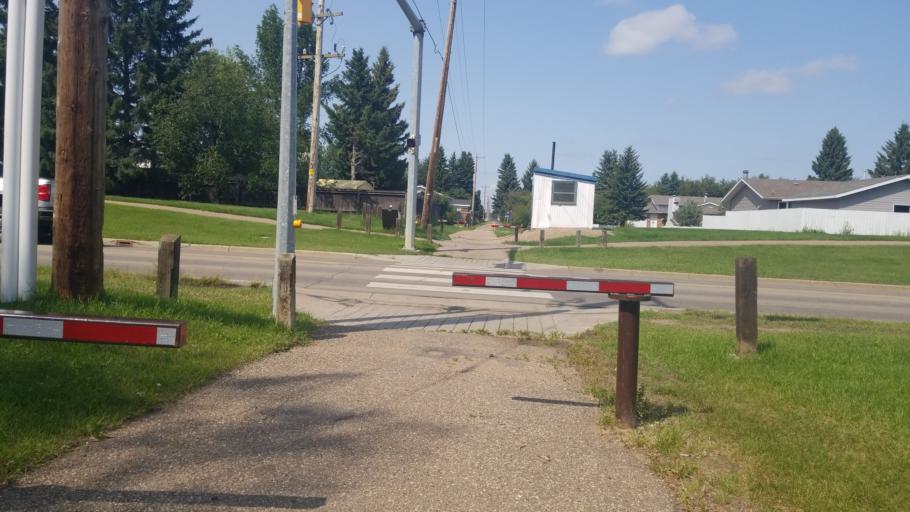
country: CA
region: Saskatchewan
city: Lloydminster
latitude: 53.2705
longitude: -110.0176
